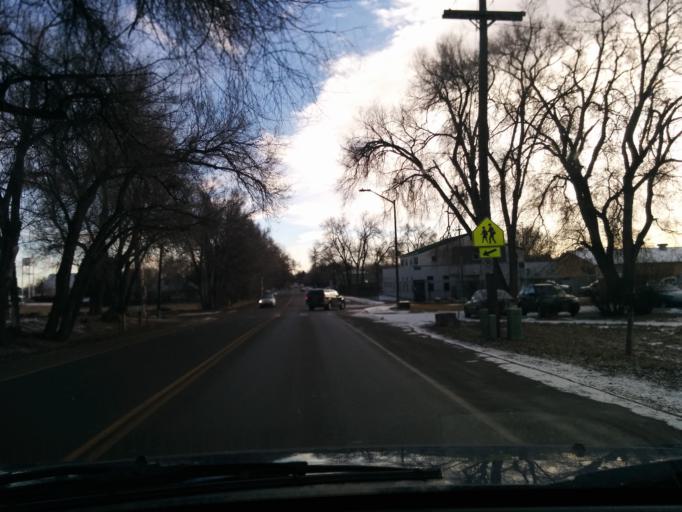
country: US
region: Colorado
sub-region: Larimer County
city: Laporte
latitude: 40.5893
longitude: -105.1243
